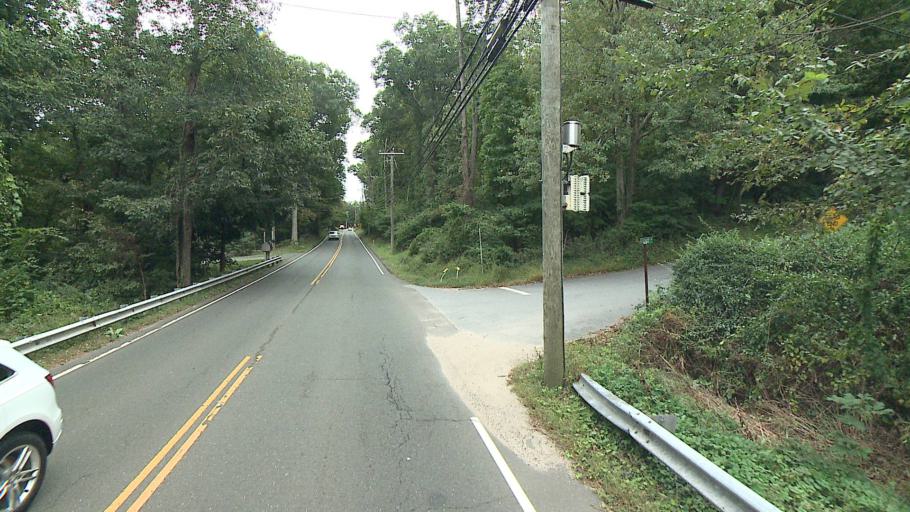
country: US
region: Connecticut
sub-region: Fairfield County
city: Wilton
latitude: 41.2057
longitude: -73.4545
